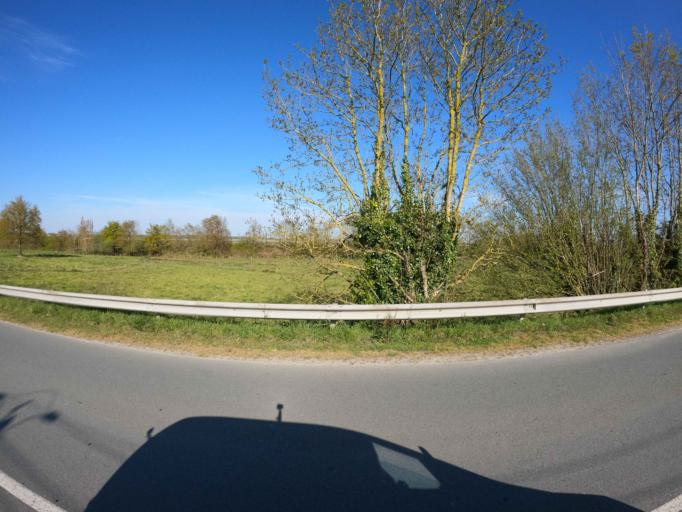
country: FR
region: Pays de la Loire
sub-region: Departement de la Vendee
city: Mortagne-sur-Sevre
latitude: 47.0005
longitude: -0.9418
